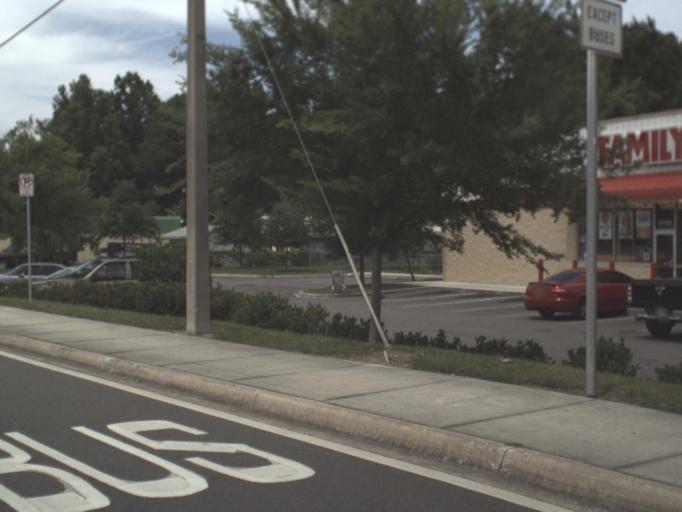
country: US
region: Florida
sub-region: Clay County
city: Bellair-Meadowbrook Terrace
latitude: 30.2265
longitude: -81.7379
